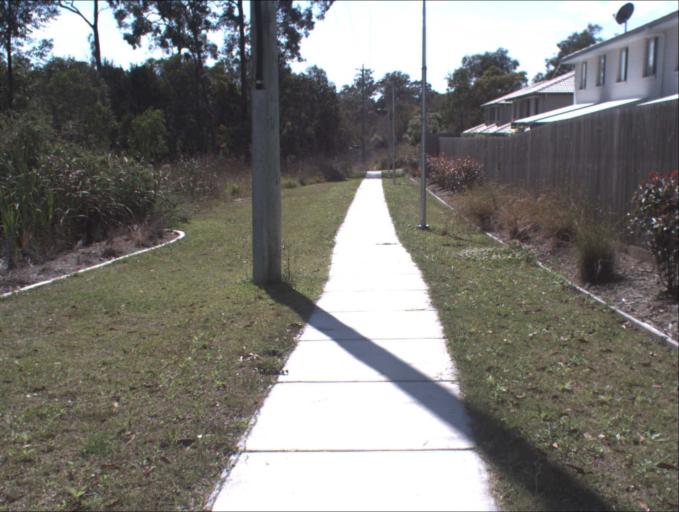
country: AU
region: Queensland
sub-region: Logan
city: Woodridge
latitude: -27.6593
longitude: 153.0853
